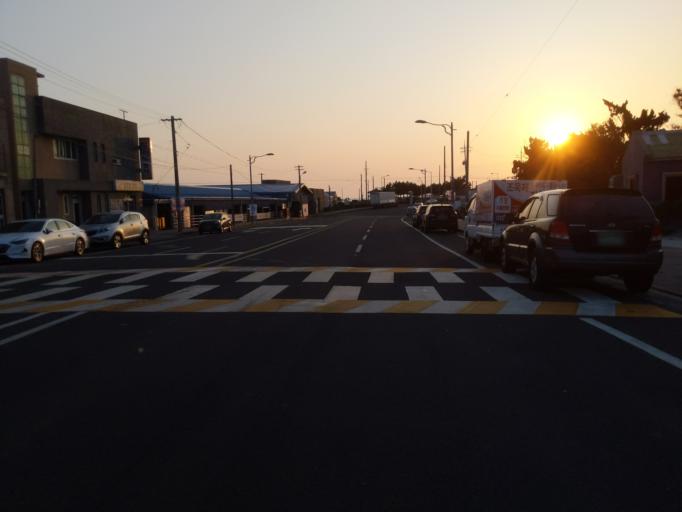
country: KR
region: Jeju-do
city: Gaigeturi
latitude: 33.2207
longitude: 126.2490
